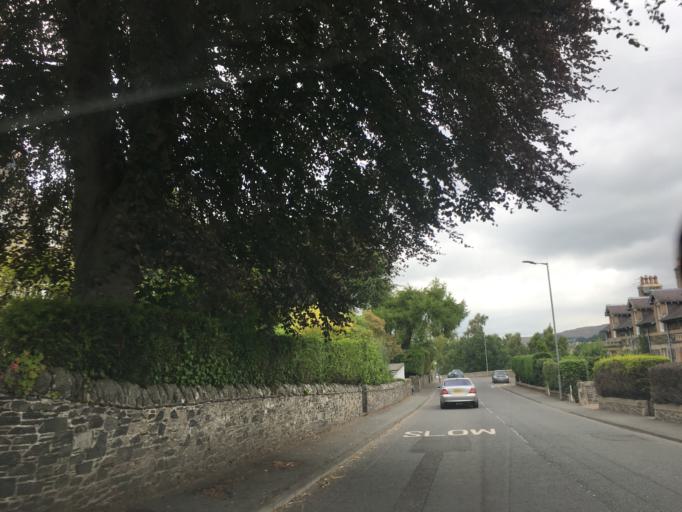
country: GB
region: Scotland
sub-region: The Scottish Borders
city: Peebles
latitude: 55.6464
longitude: -3.1882
